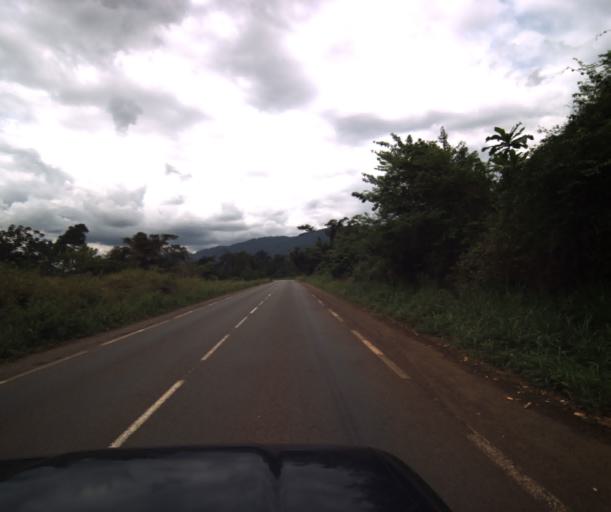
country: CM
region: Centre
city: Eseka
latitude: 3.8804
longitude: 10.8111
